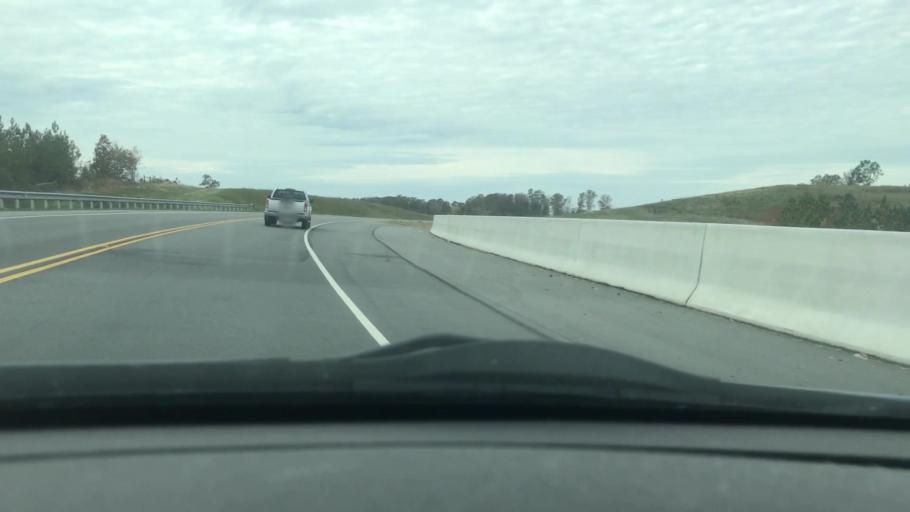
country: US
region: North Carolina
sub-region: Randolph County
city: Asheboro
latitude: 35.6975
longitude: -79.8691
